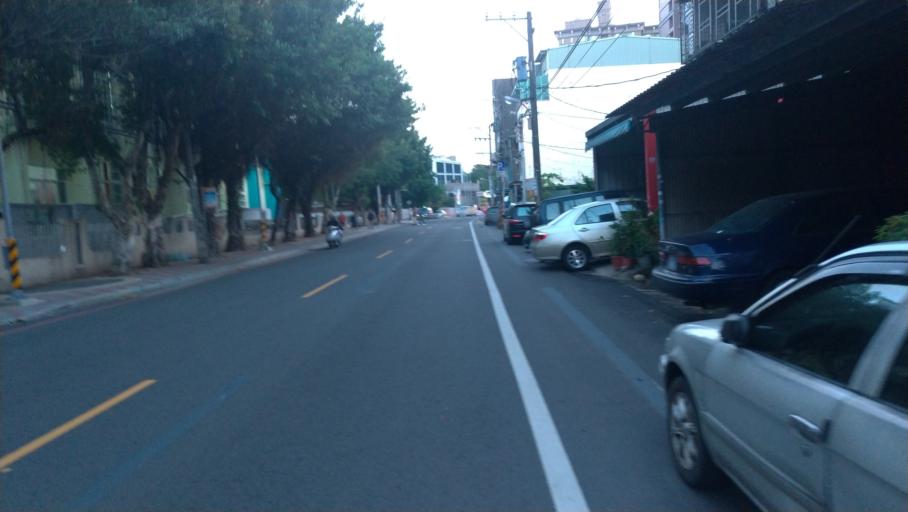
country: TW
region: Taiwan
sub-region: Taoyuan
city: Taoyuan
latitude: 24.9830
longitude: 121.3147
